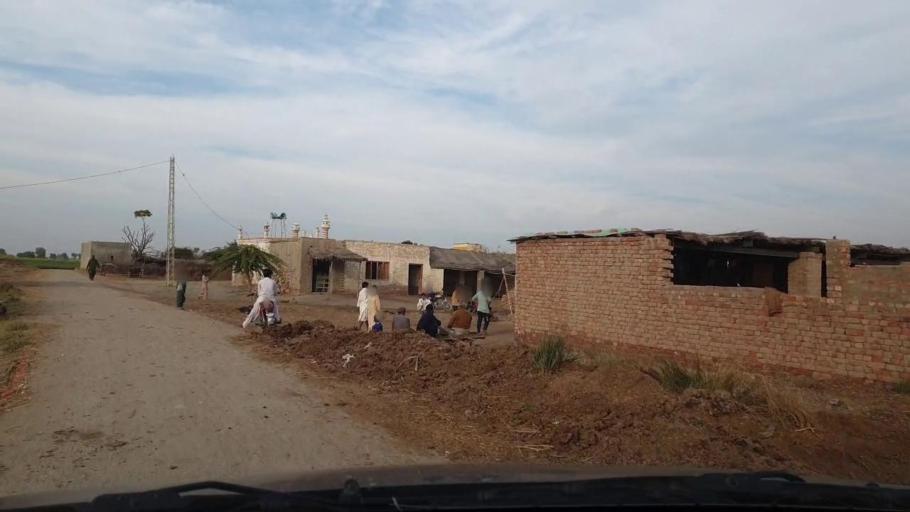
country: PK
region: Sindh
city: Khadro
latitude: 26.1680
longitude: 68.7265
